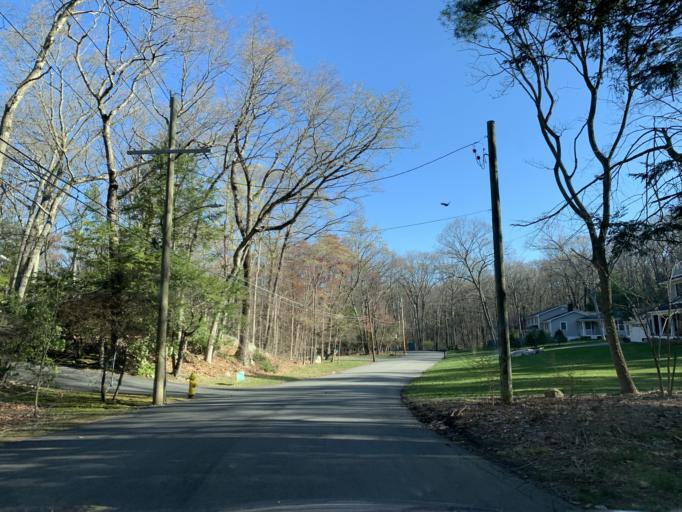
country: US
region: Massachusetts
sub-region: Norfolk County
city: Westwood
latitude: 42.2359
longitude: -71.2021
